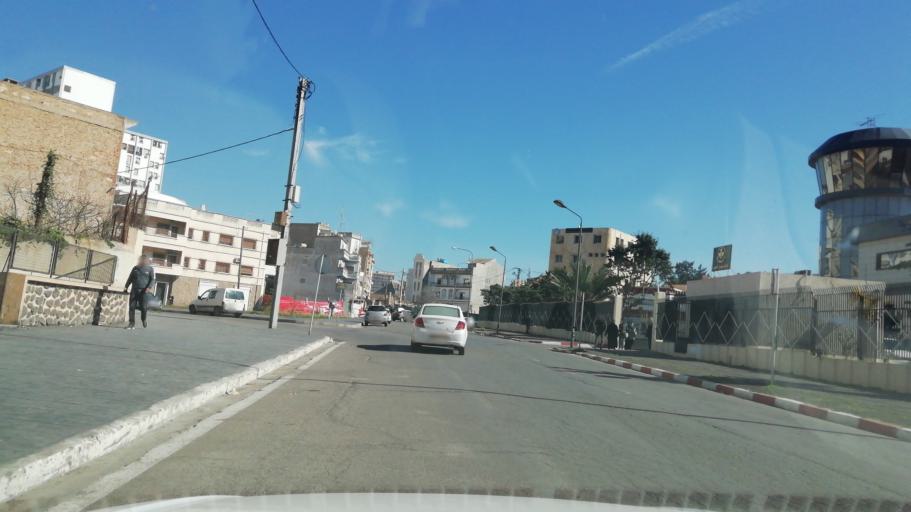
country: DZ
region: Oran
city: Oran
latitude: 35.6978
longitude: -0.6296
